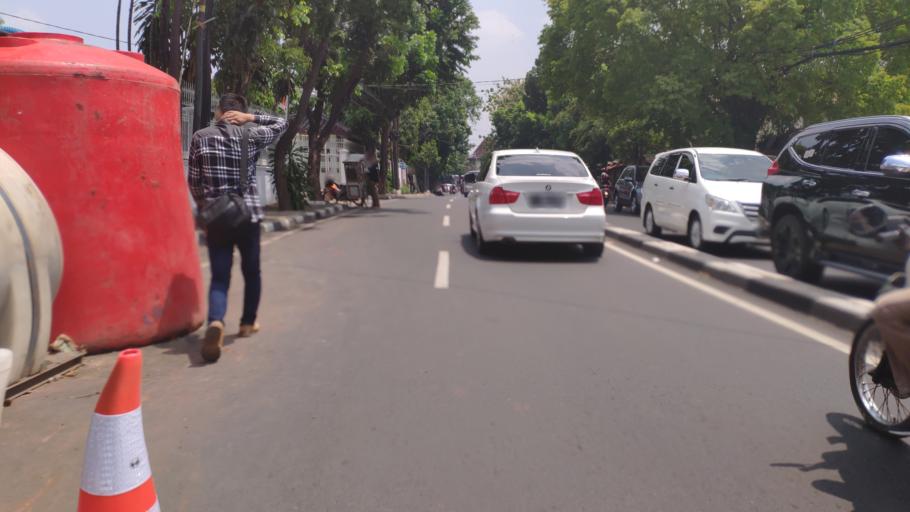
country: ID
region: Jakarta Raya
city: Jakarta
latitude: -6.2761
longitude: 106.8218
